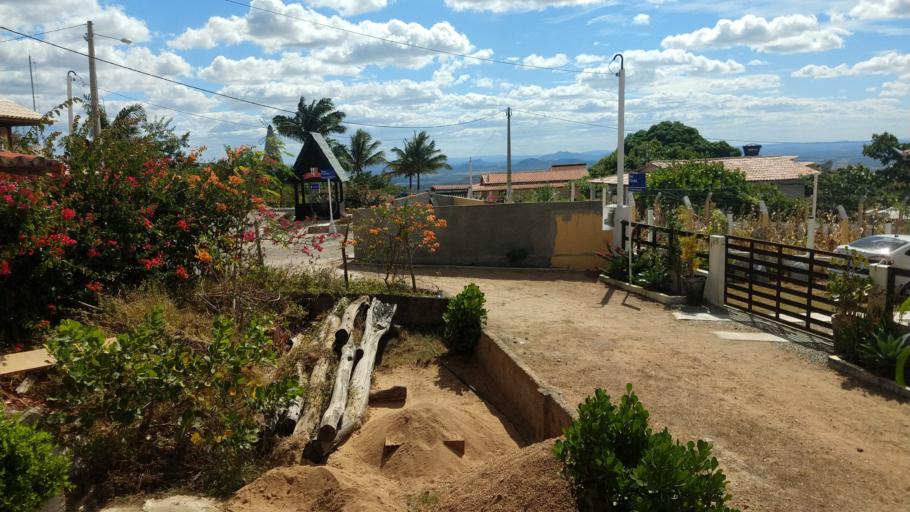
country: BR
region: Rio Grande do Norte
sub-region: Sao Jose Do Campestre
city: Sao Jose do Campestre
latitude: -6.4186
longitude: -35.7646
